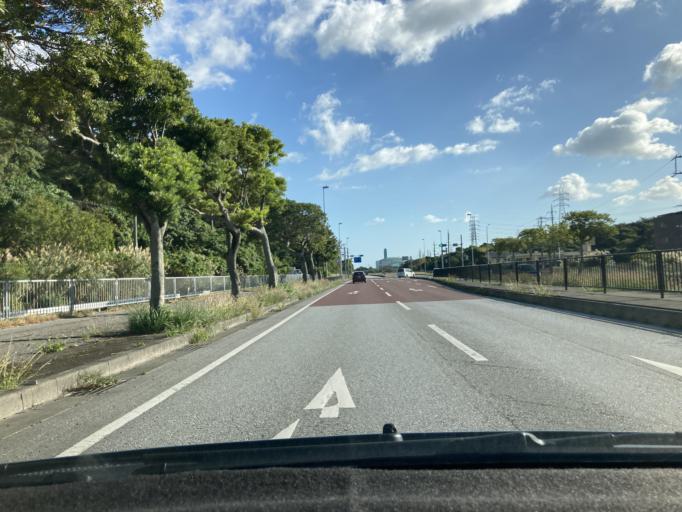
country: JP
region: Okinawa
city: Ishikawa
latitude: 26.4097
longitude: 127.8199
